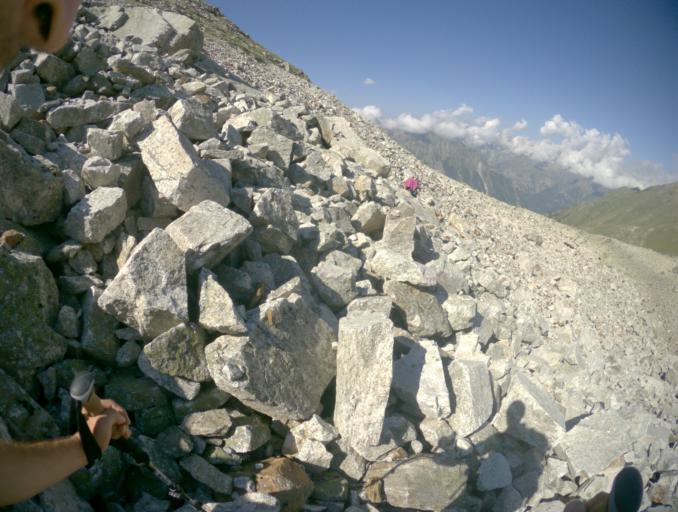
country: RU
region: Karachayevo-Cherkesiya
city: Uchkulan
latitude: 43.3071
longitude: 42.0651
